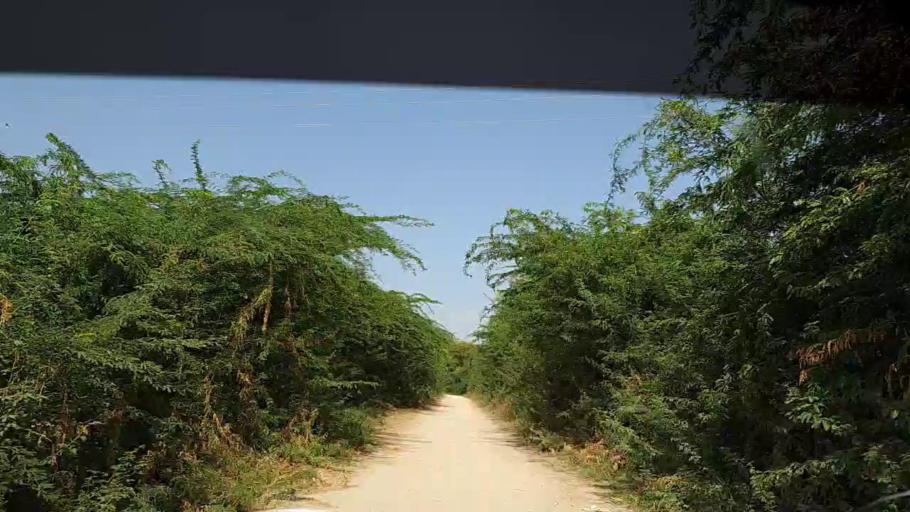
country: PK
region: Sindh
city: Badin
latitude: 24.5922
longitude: 68.7975
